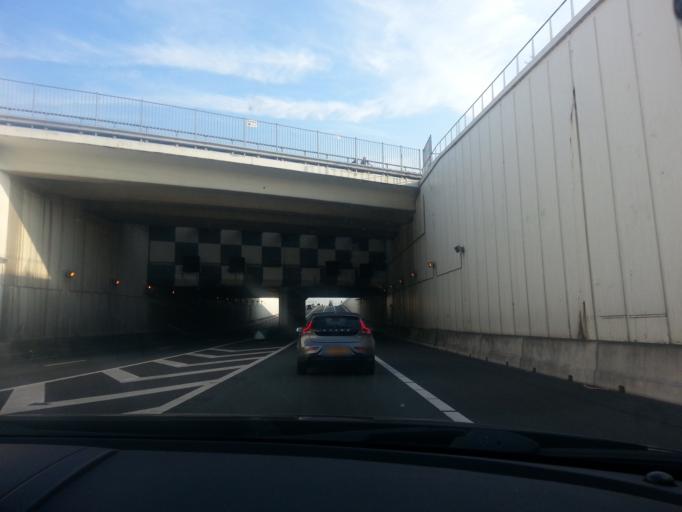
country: NL
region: South Holland
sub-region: Gemeente Kaag en Braassem
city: Oude Wetering
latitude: 52.2162
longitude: 4.6271
